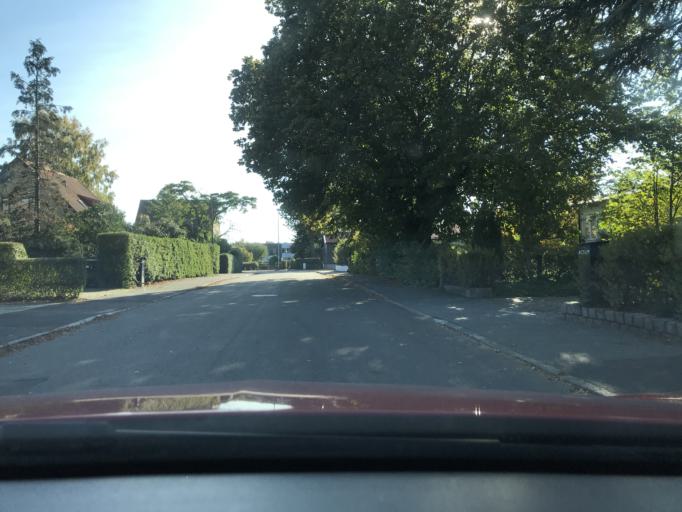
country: SE
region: Skane
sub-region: Lunds Kommun
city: Lund
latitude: 55.6908
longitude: 13.2012
